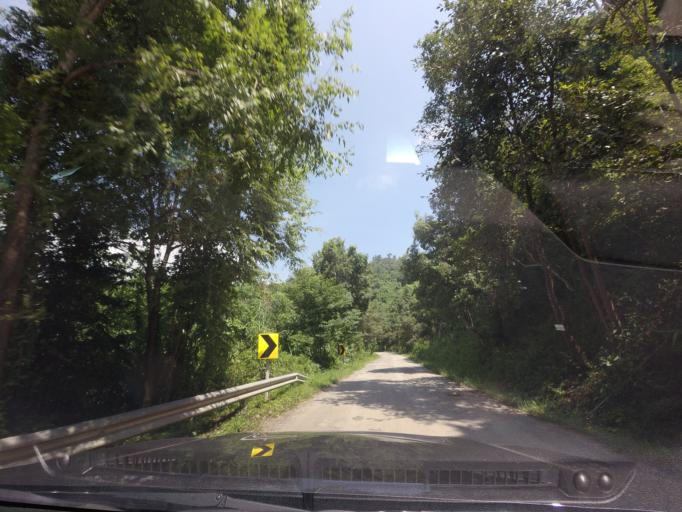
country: TH
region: Loei
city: Na Haeo
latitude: 17.6100
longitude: 100.8945
